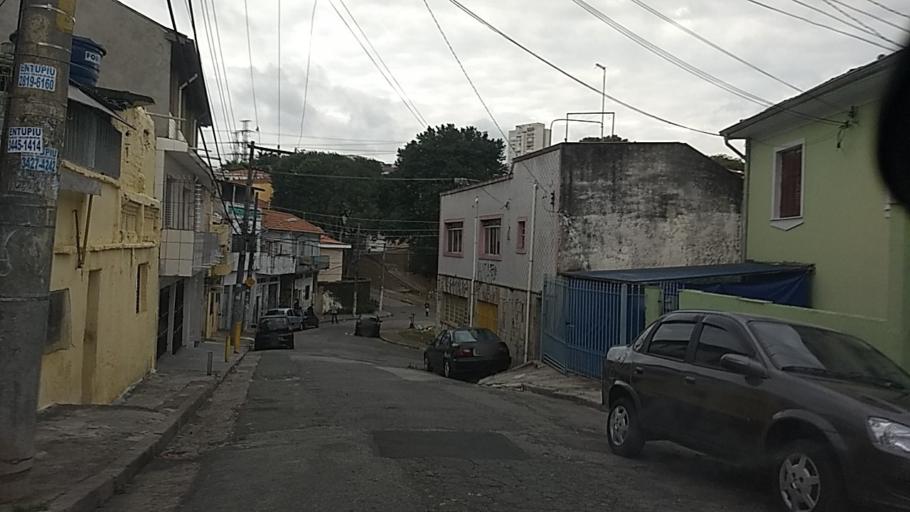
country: BR
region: Sao Paulo
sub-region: Sao Paulo
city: Sao Paulo
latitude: -23.5013
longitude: -46.6002
